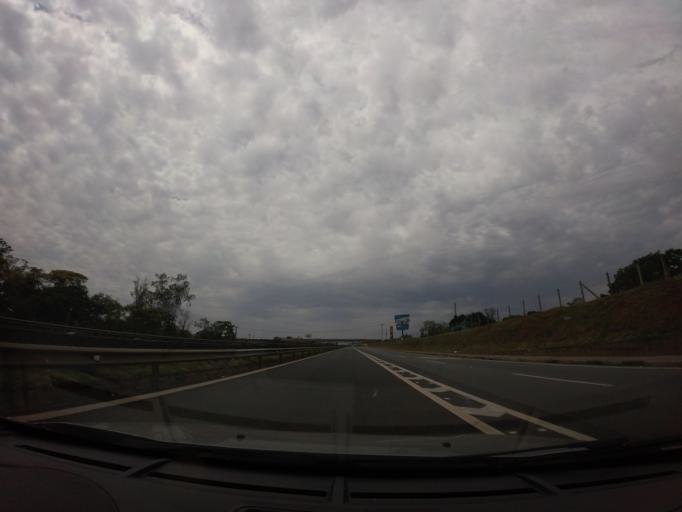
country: BR
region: Sao Paulo
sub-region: Hortolandia
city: Hortolandia
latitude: -22.8392
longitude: -47.1715
